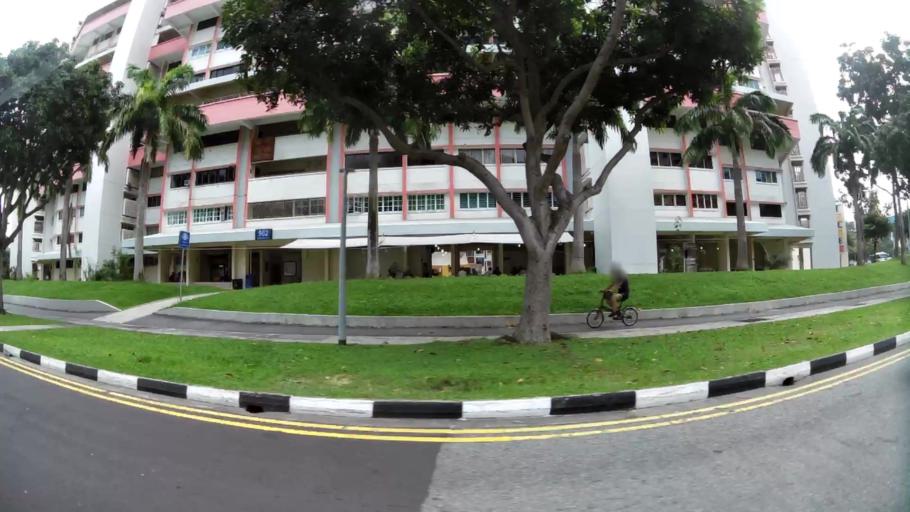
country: SG
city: Singapore
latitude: 1.3514
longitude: 103.9389
